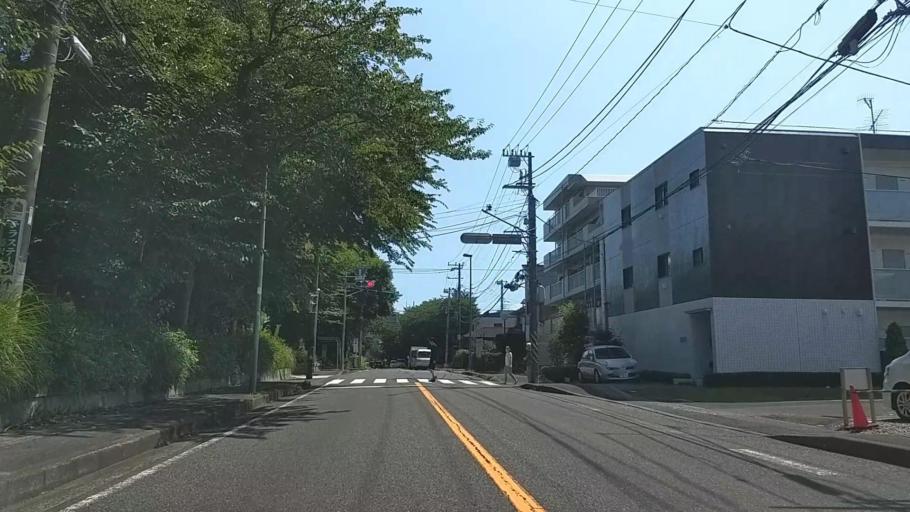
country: JP
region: Kanagawa
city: Fujisawa
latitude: 35.3592
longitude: 139.4939
